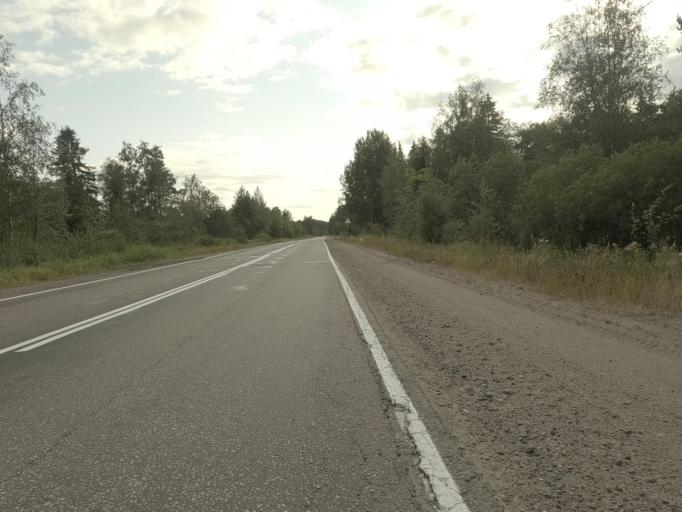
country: RU
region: Leningrad
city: Kamennogorsk
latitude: 60.8763
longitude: 29.0047
